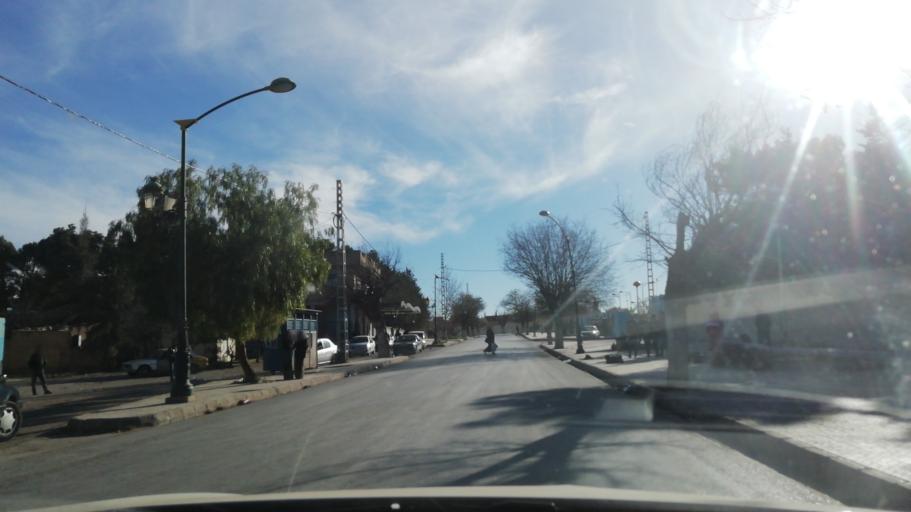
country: DZ
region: Tlemcen
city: Sebdou
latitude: 34.6366
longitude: -1.3332
